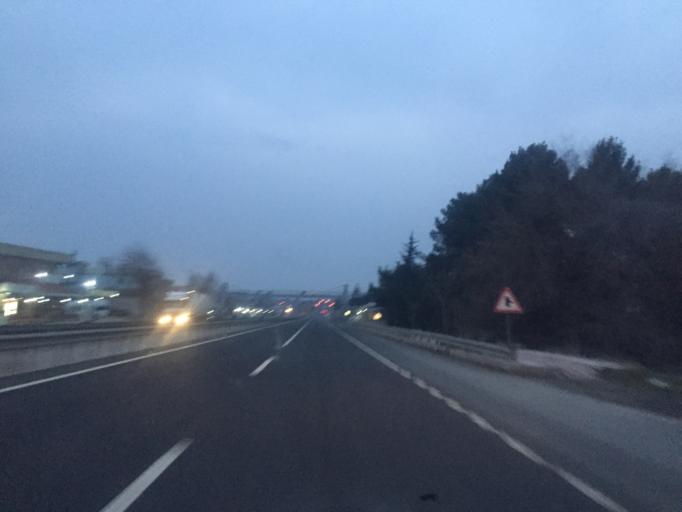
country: TR
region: Sanliurfa
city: Camlidere
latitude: 37.1543
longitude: 39.0626
